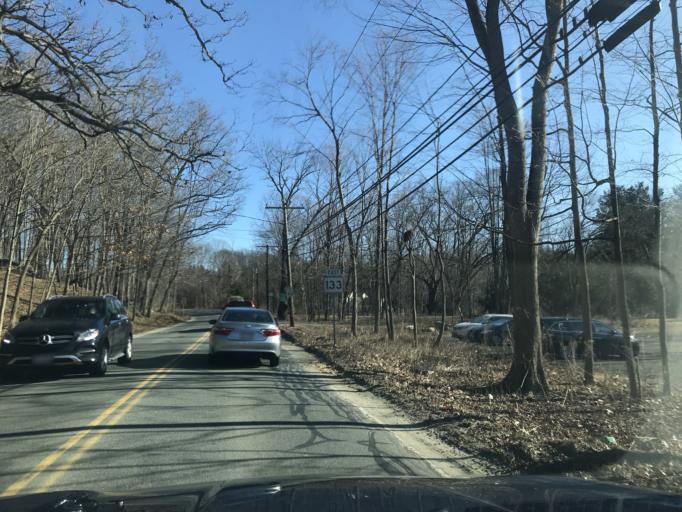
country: US
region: Massachusetts
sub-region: Essex County
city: Groveland
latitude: 42.7075
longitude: -71.0635
